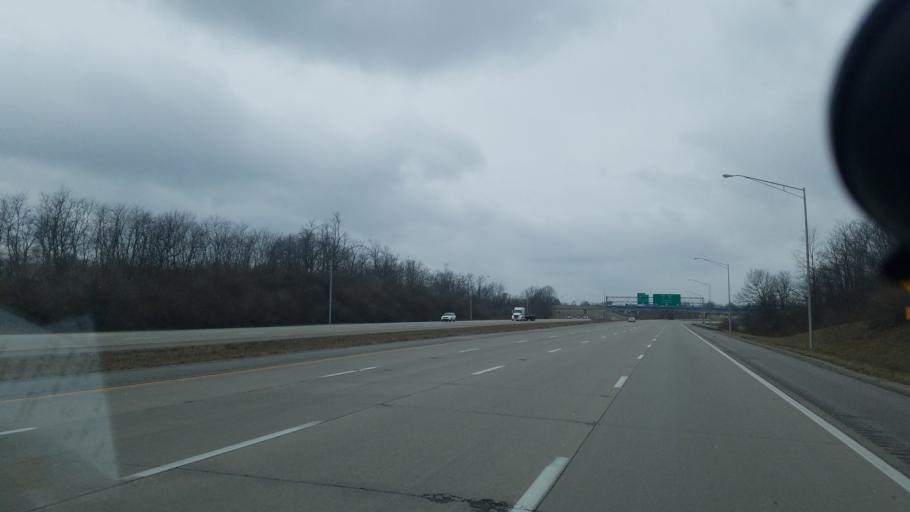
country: US
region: Kentucky
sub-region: Fayette County
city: Lexington-Fayette
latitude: 38.0573
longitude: -84.4195
